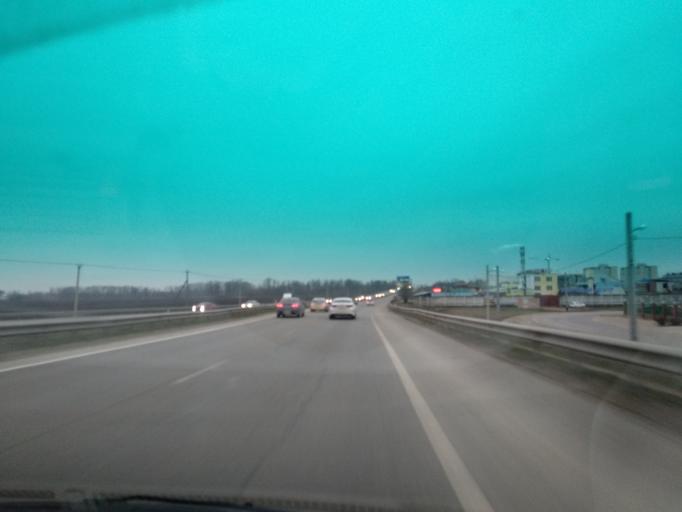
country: RU
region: Krasnodarskiy
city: Pashkovskiy
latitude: 45.0521
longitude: 39.1302
